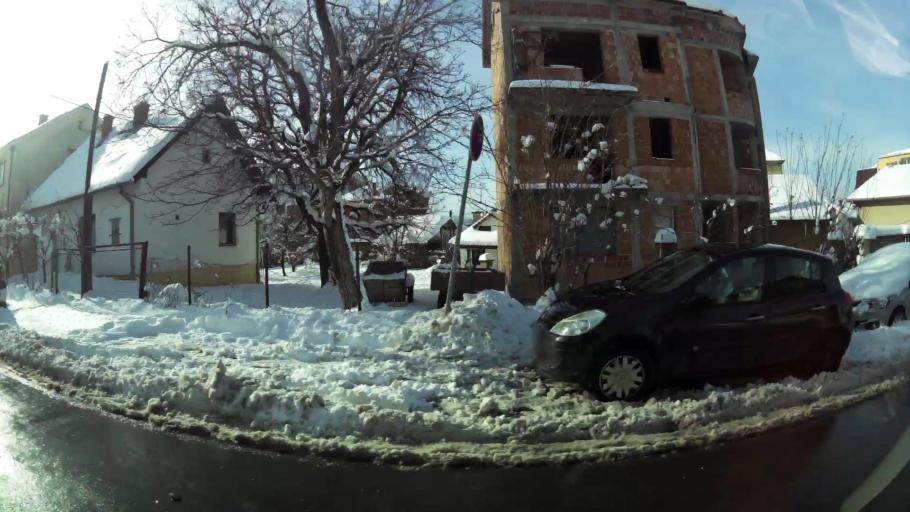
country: RS
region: Central Serbia
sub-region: Belgrade
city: Zvezdara
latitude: 44.7939
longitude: 20.5342
